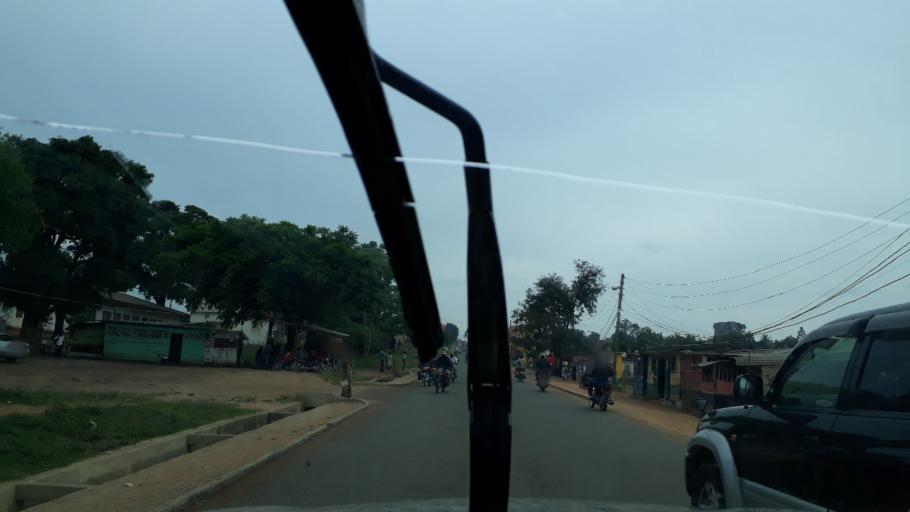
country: CD
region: Eastern Province
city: Bunia
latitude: 1.5607
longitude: 30.2426
